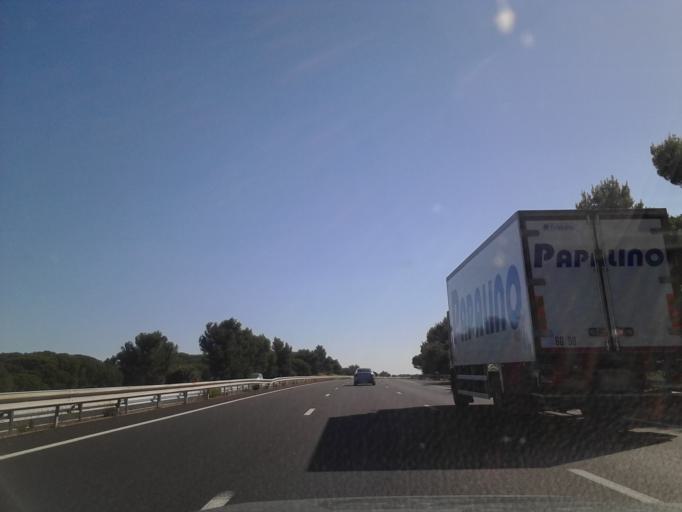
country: FR
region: Languedoc-Roussillon
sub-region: Departement de l'Aude
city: Vinassan
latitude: 43.2256
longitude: 3.0999
